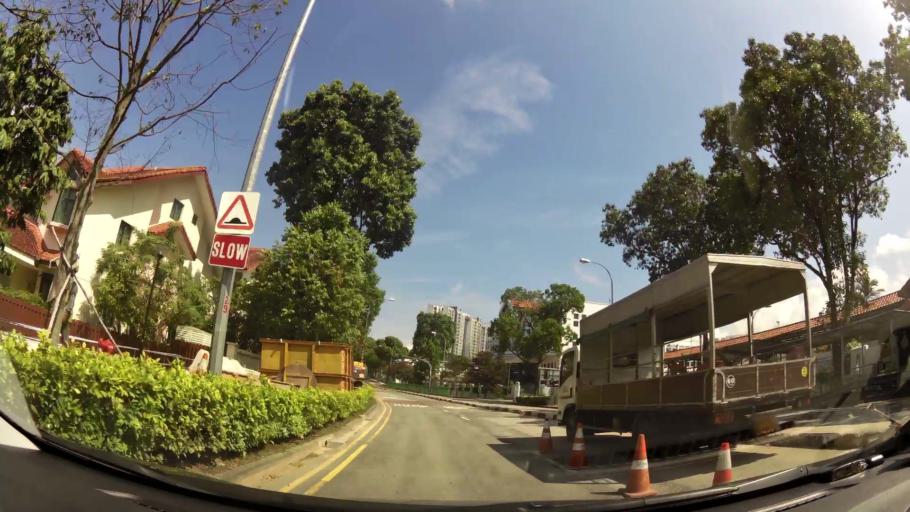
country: SG
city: Singapore
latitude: 1.3719
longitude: 103.8330
